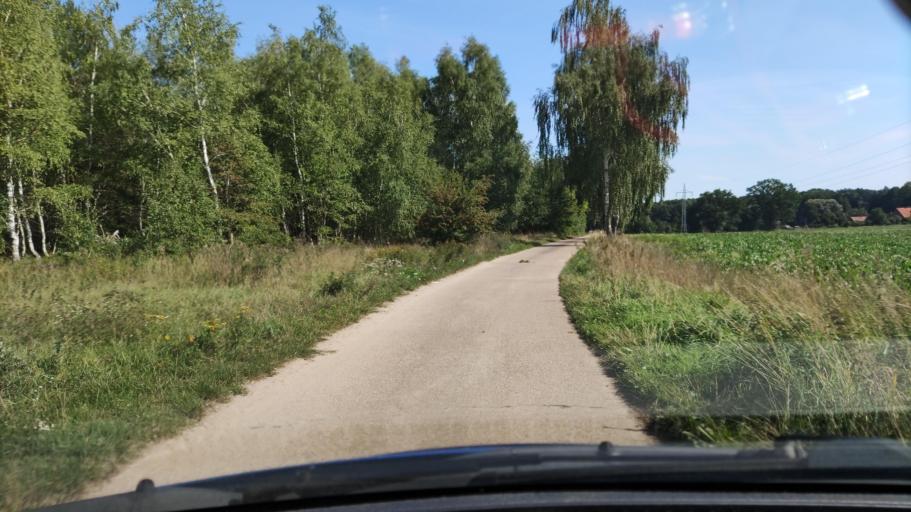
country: DE
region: Lower Saxony
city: Gohrde
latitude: 53.1394
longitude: 10.9486
